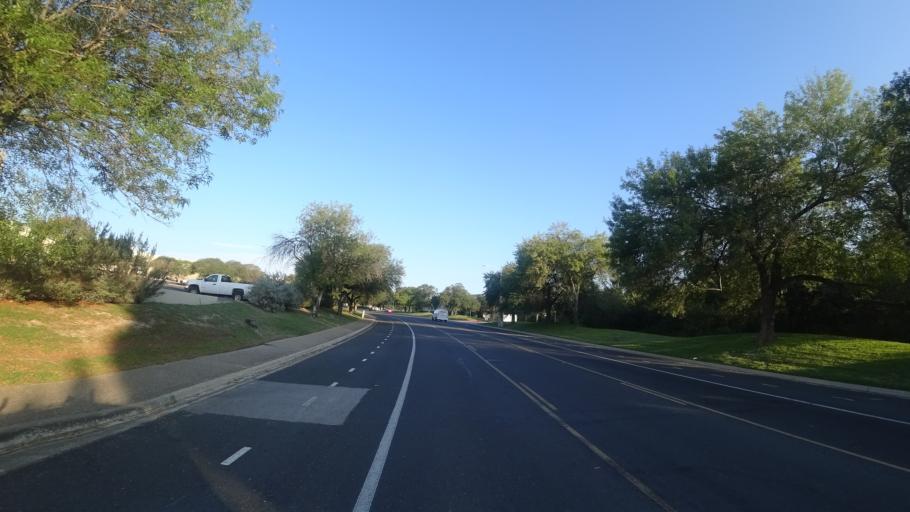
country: US
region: Texas
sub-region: Travis County
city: Austin
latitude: 30.3355
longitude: -97.6807
